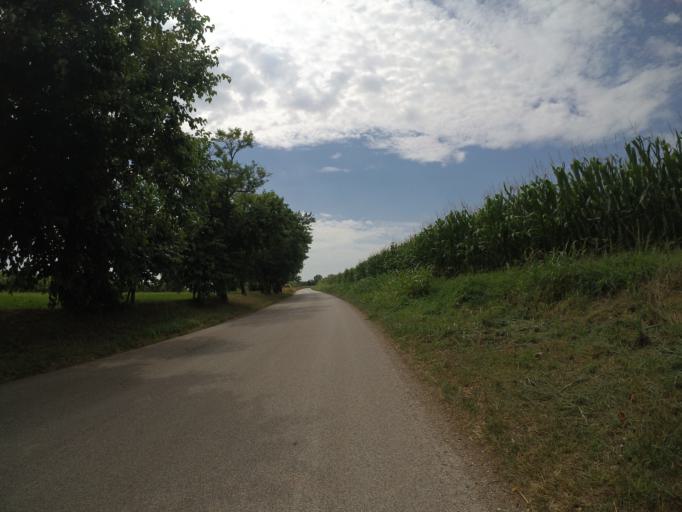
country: IT
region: Friuli Venezia Giulia
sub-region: Provincia di Udine
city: Basiliano
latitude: 45.9789
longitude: 13.0875
